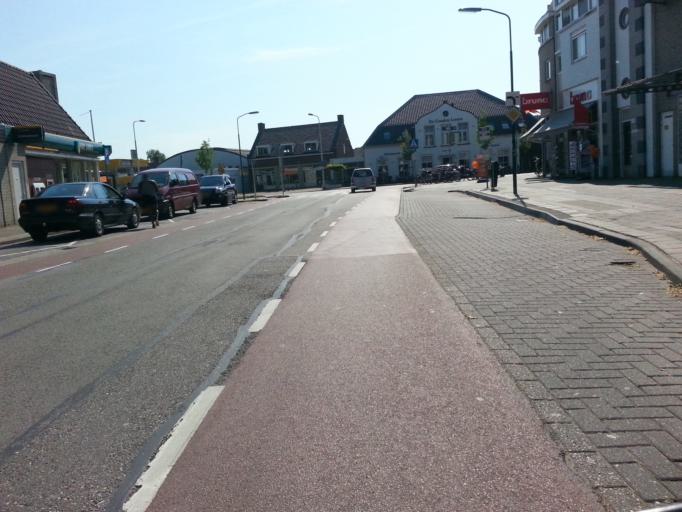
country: NL
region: Utrecht
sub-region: Gemeente Wijk bij Duurstede
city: Wijk bij Duurstede
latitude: 51.9747
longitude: 5.3438
